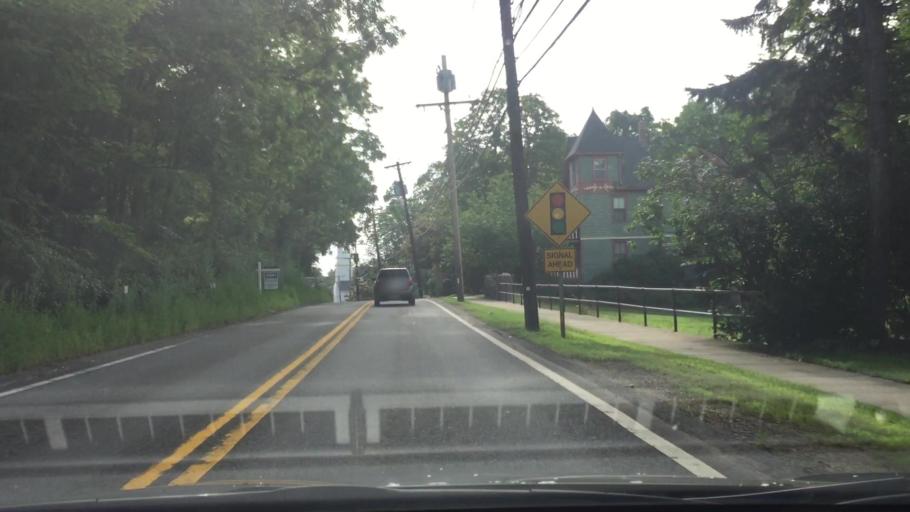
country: US
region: Massachusetts
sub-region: Middlesex County
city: Acton
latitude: 42.4764
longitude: -71.4778
